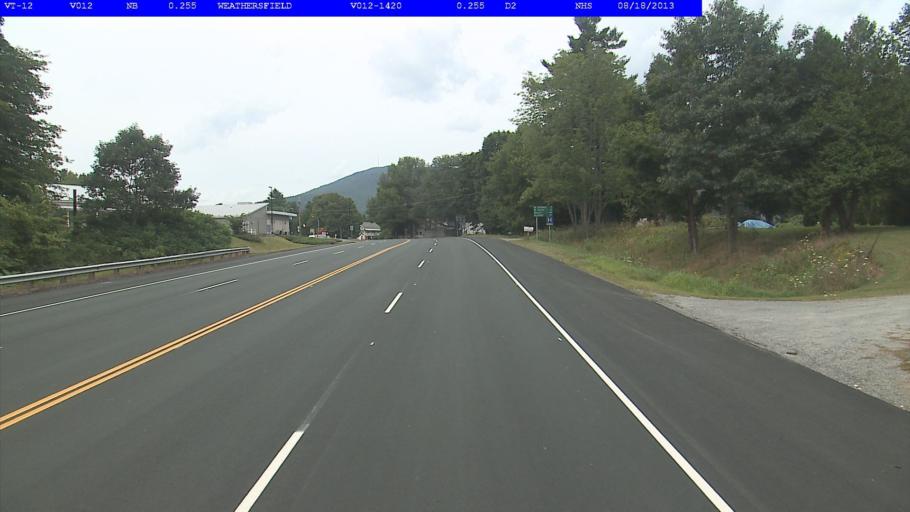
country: US
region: New Hampshire
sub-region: Sullivan County
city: Claremont
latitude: 43.4052
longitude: -72.4054
